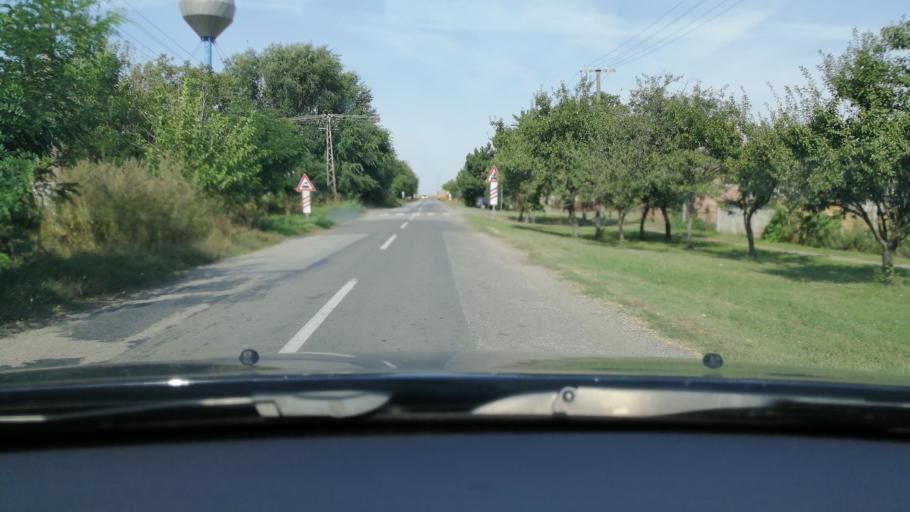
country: RS
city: Orlovat
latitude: 45.2491
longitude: 20.5798
